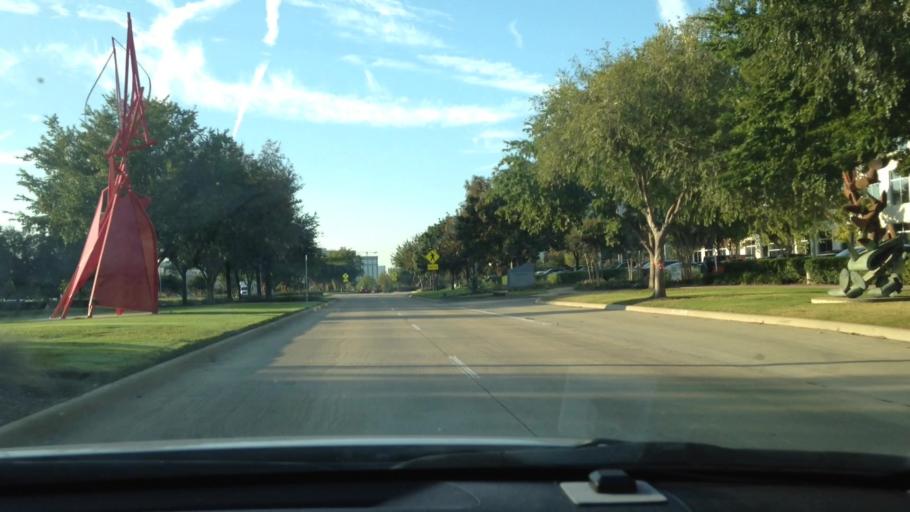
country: US
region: Texas
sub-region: Collin County
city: Frisco
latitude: 33.1060
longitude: -96.8265
